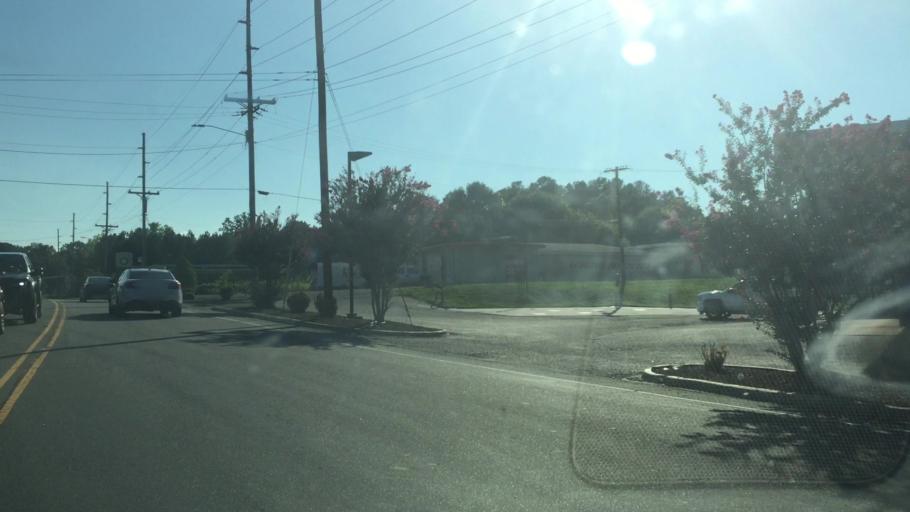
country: US
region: North Carolina
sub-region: Cabarrus County
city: Concord
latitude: 35.4144
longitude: -80.6134
